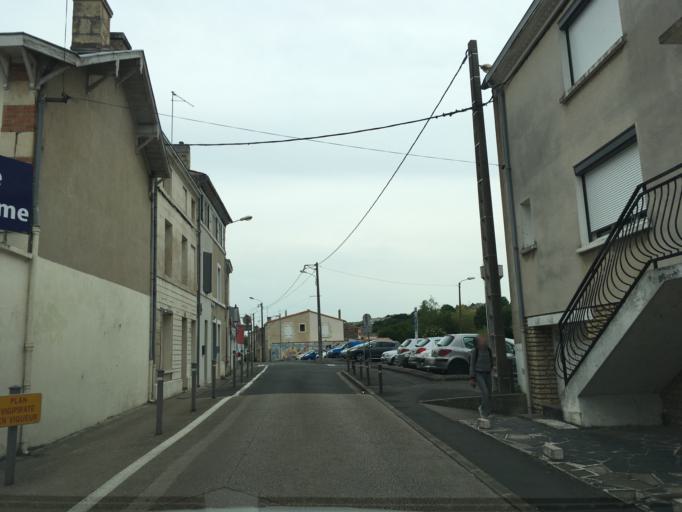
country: FR
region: Poitou-Charentes
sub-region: Departement des Deux-Sevres
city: Niort
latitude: 46.3287
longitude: -0.4656
